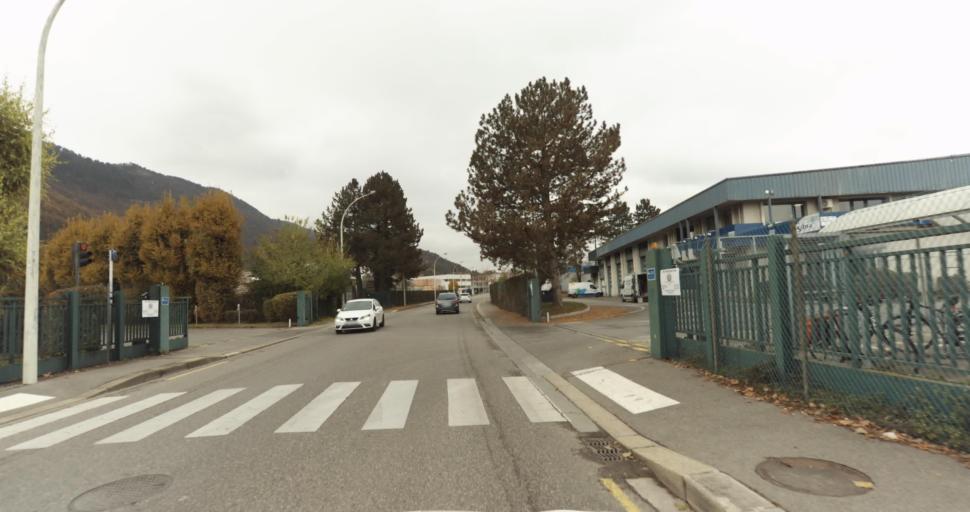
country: FR
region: Rhone-Alpes
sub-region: Departement de la Haute-Savoie
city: Annecy
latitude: 45.8878
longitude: 6.1192
